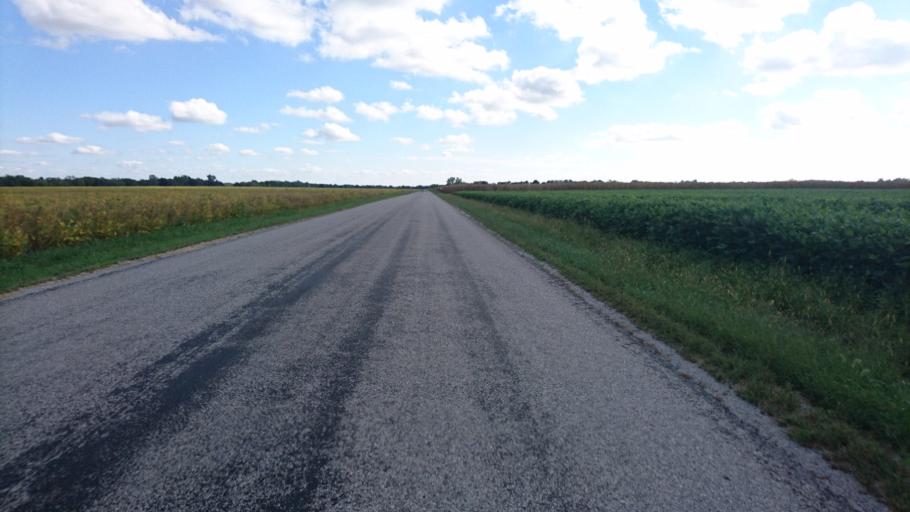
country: US
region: Illinois
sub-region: Macoupin County
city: Mount Olive
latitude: 39.0145
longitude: -89.7314
